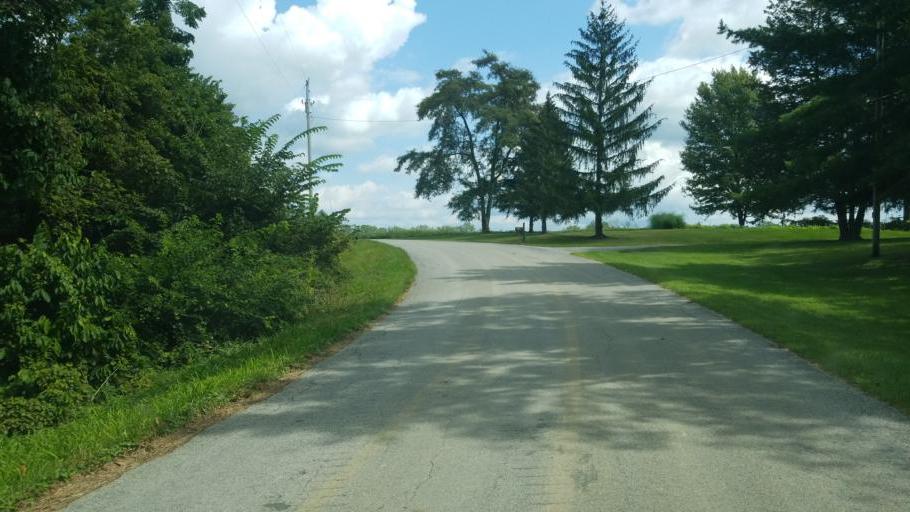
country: US
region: Ohio
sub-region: Huron County
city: Monroeville
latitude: 41.1714
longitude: -82.7520
